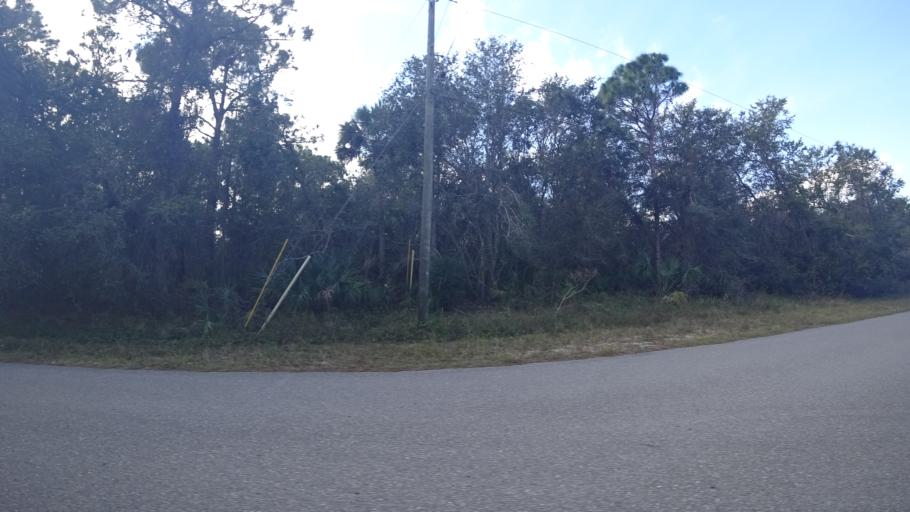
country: US
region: Florida
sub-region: Charlotte County
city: Port Charlotte
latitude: 27.0493
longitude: -82.1237
